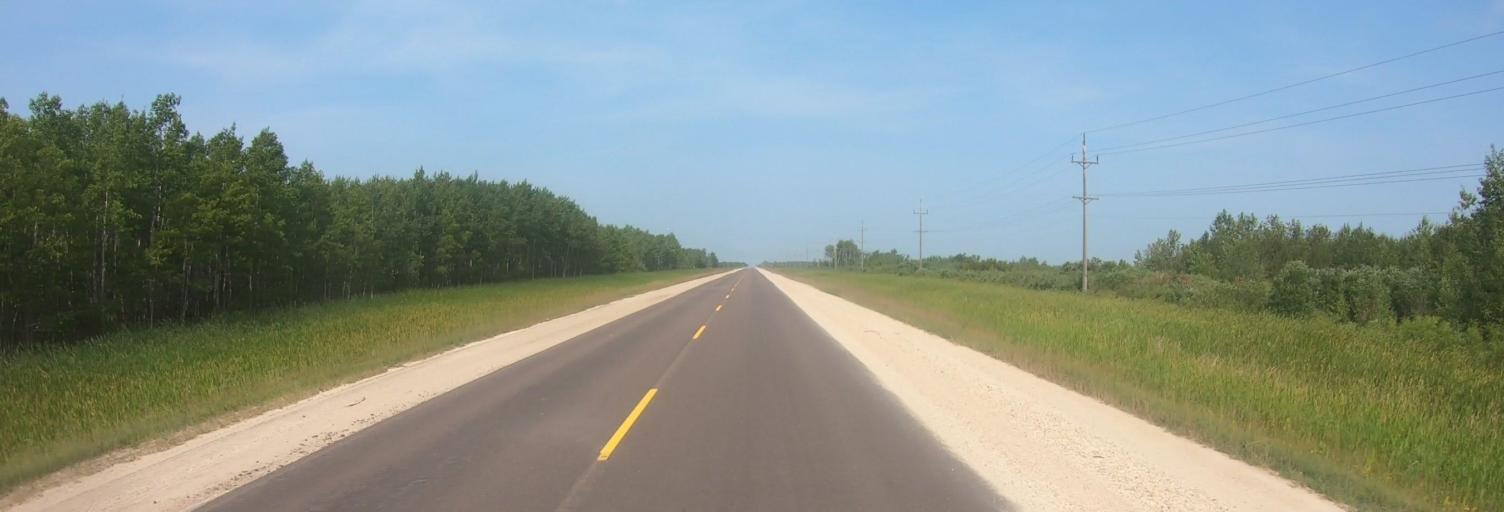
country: CA
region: Manitoba
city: La Broquerie
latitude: 49.2710
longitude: -96.4831
